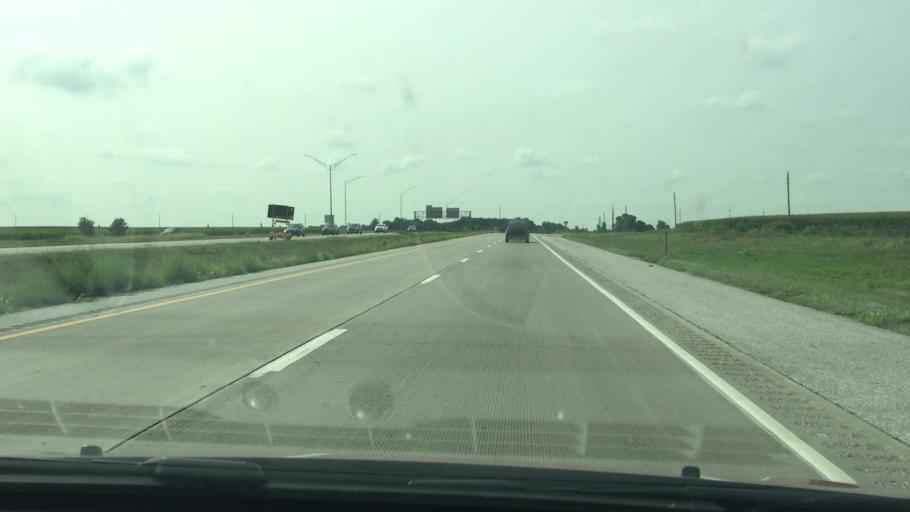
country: US
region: Iowa
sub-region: Scott County
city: Walcott
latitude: 41.5888
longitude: -90.6761
